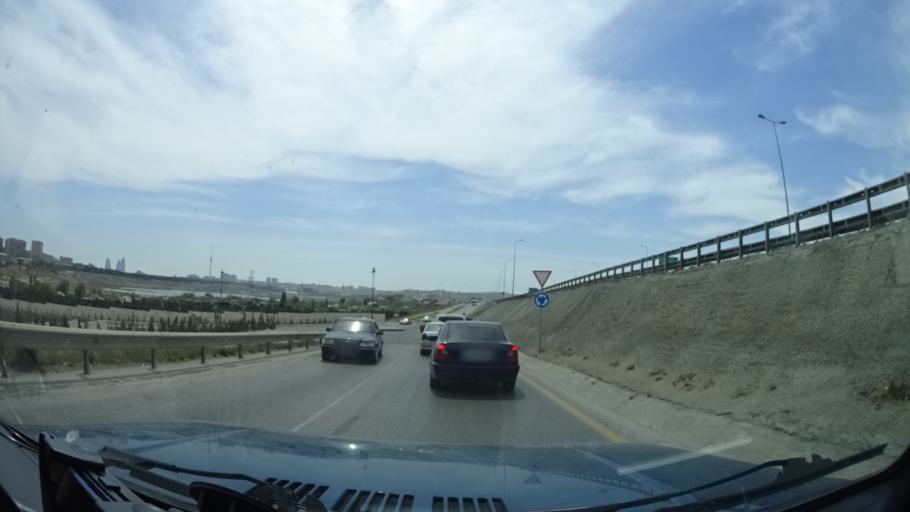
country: AZ
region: Baki
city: Badamdar
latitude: 40.3755
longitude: 49.7907
